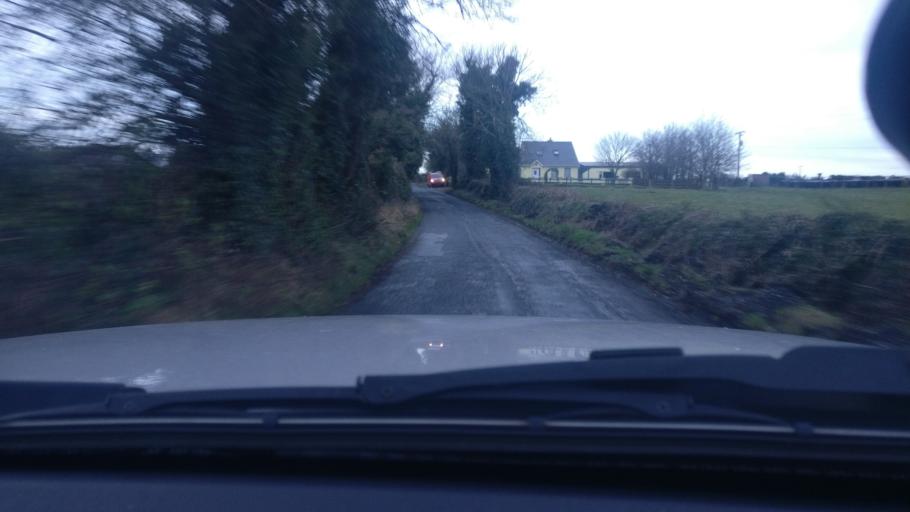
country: IE
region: Connaught
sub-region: County Galway
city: Loughrea
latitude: 53.1731
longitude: -8.5085
